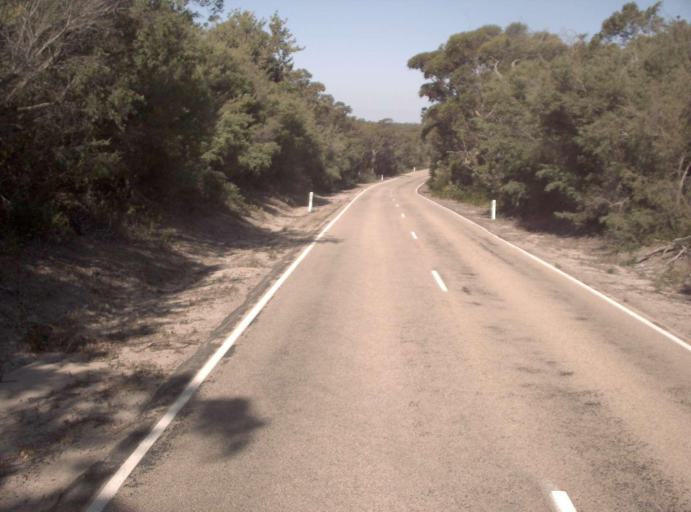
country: AU
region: Victoria
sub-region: East Gippsland
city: Lakes Entrance
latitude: -37.7980
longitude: 148.6934
